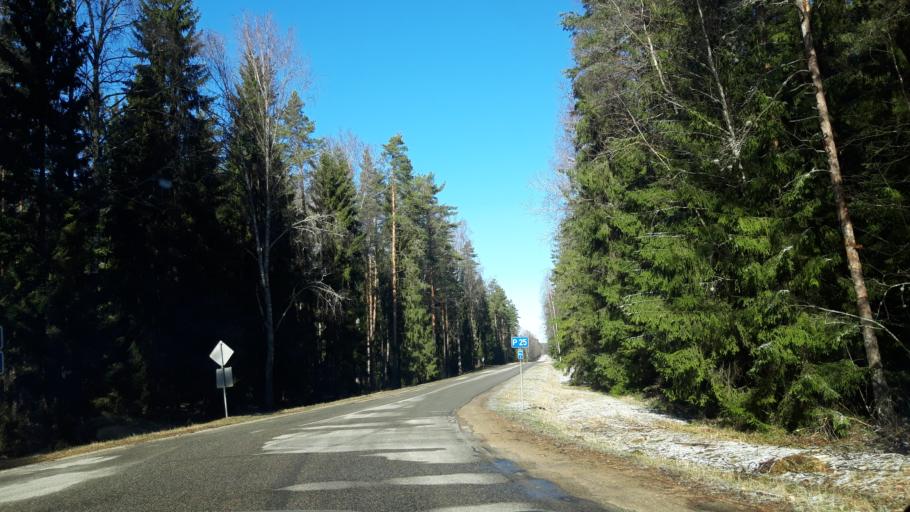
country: LV
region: Strenci
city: Strenci
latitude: 57.5999
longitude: 25.7169
